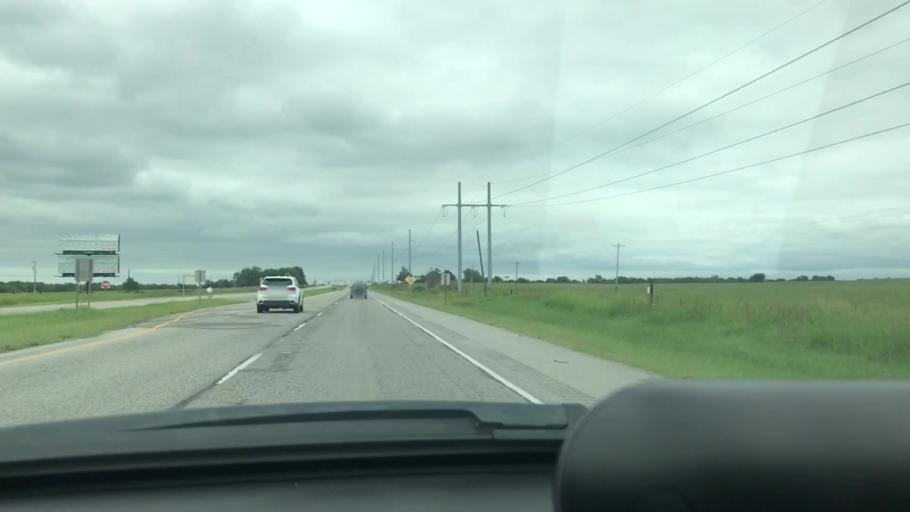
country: US
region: Oklahoma
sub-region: Wagoner County
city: Wagoner
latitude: 36.0091
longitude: -95.3685
